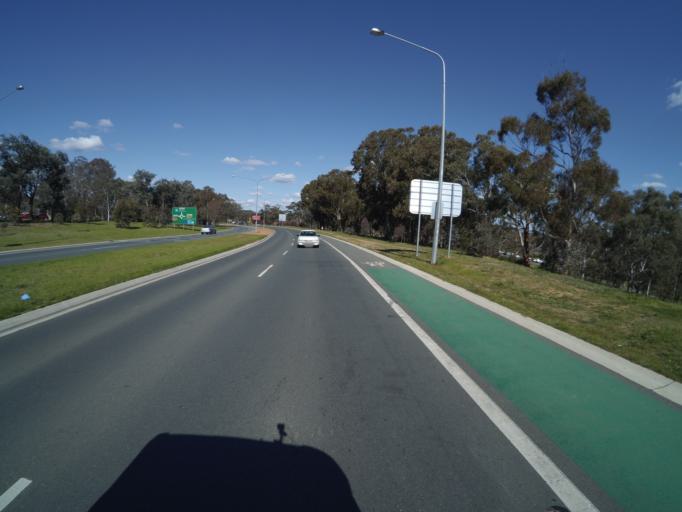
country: AU
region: Australian Capital Territory
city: Forrest
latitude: -35.3016
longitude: 149.1496
